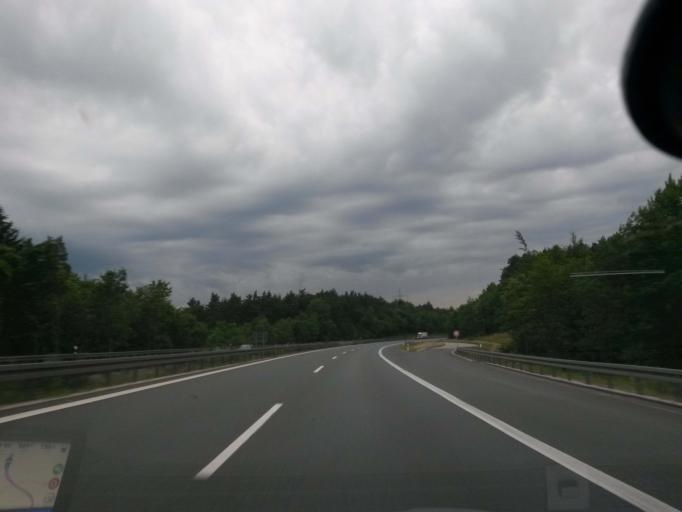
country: DE
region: Bavaria
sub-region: Regierungsbezirk Mittelfranken
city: Altdorf
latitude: 49.4006
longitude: 11.3869
